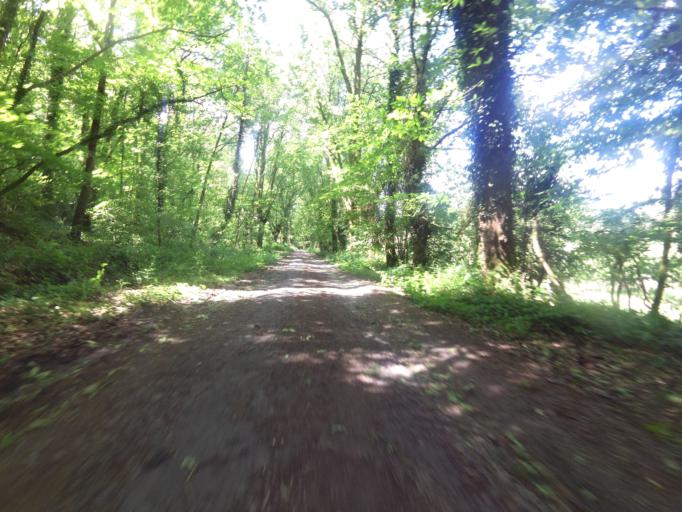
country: FR
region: Brittany
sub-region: Departement du Morbihan
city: Pluherlin
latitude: 47.7023
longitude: -2.3490
